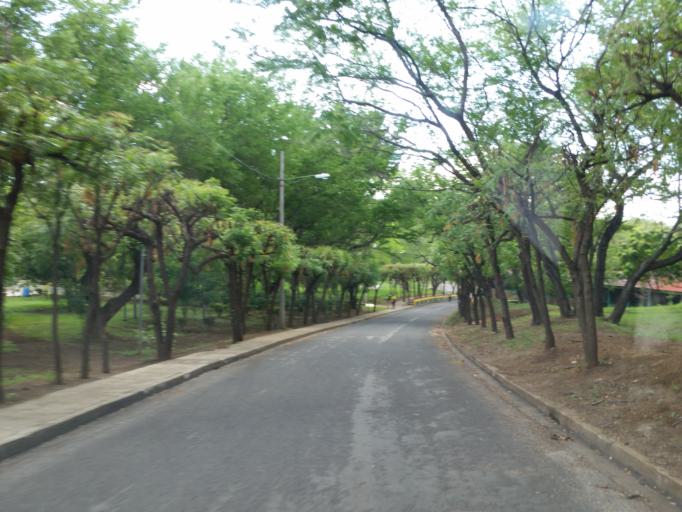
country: NI
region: Managua
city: Managua
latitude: 12.1046
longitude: -86.2704
